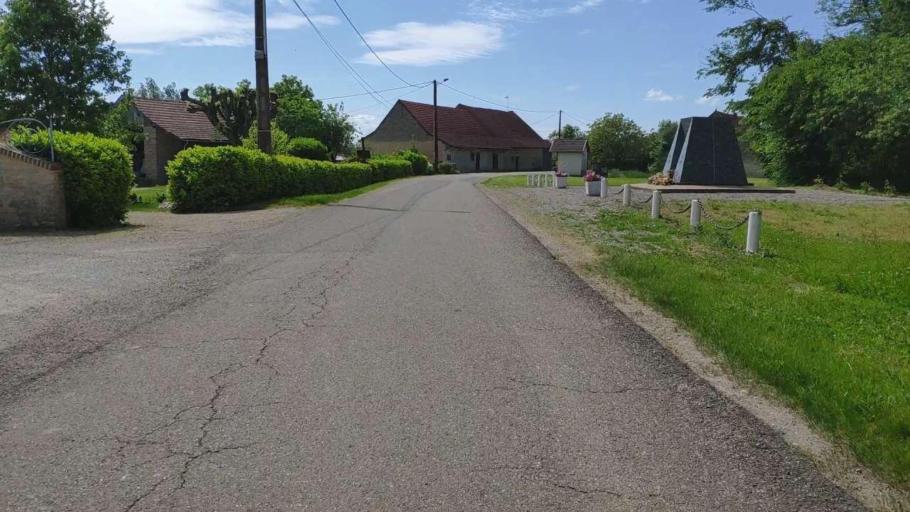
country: FR
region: Franche-Comte
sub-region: Departement du Jura
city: Bletterans
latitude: 46.7062
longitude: 5.4112
